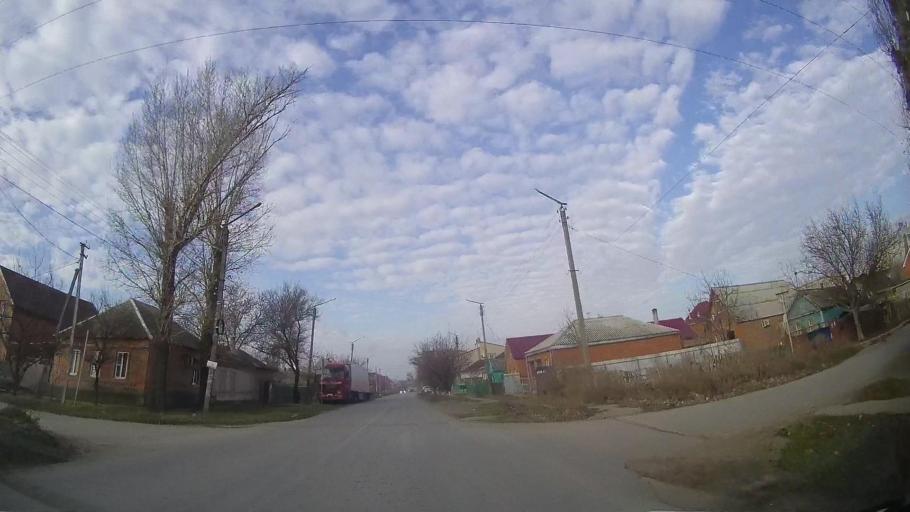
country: RU
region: Rostov
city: Bataysk
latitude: 47.1336
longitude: 39.7717
